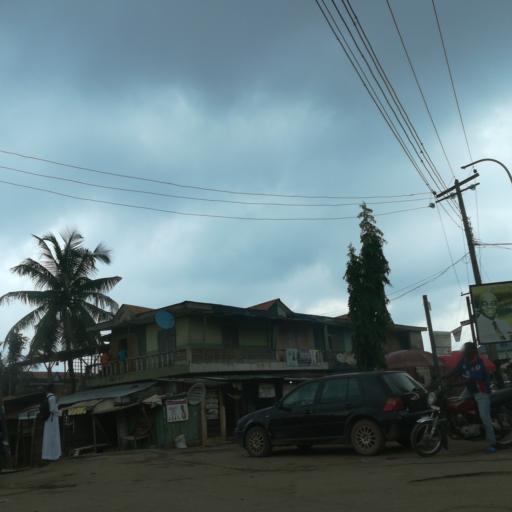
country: NG
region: Lagos
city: Agege
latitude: 6.5862
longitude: 3.3060
